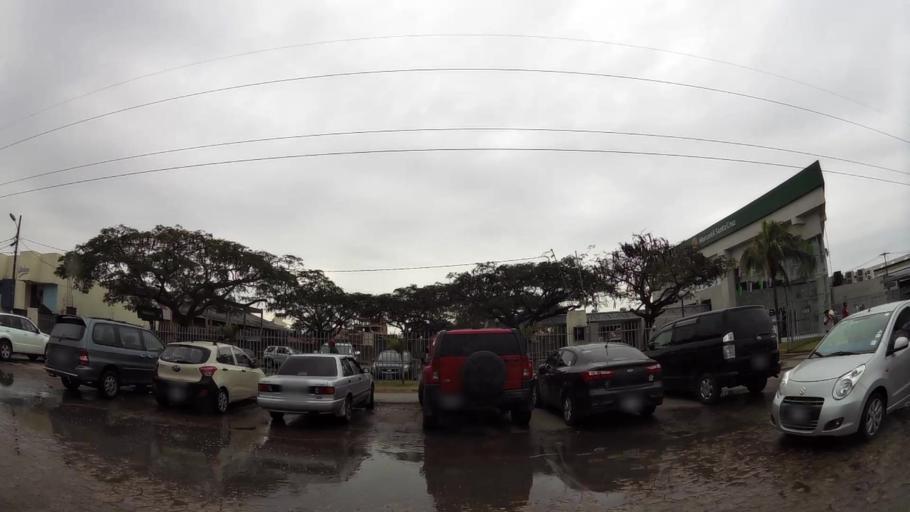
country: BO
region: Santa Cruz
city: Santa Cruz de la Sierra
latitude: -17.7625
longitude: -63.1640
